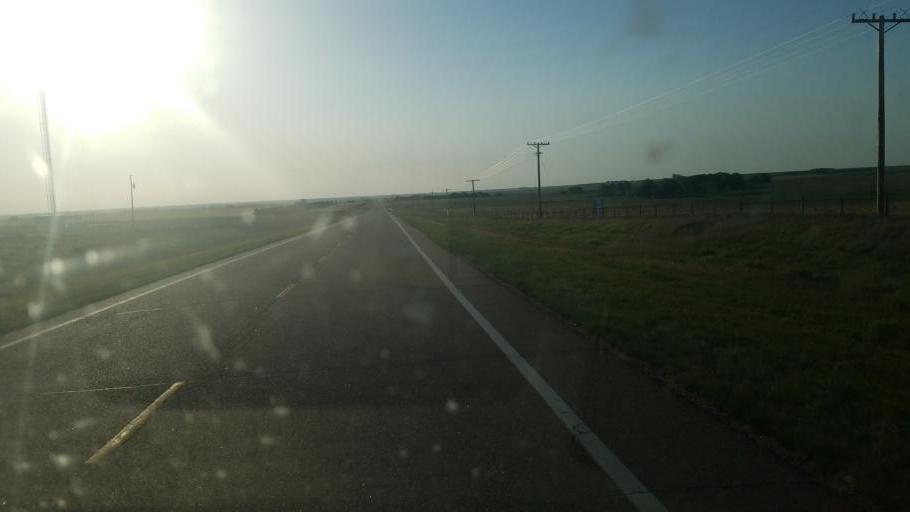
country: US
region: Kansas
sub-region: Finney County
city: Garden City
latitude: 38.0600
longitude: -100.6079
